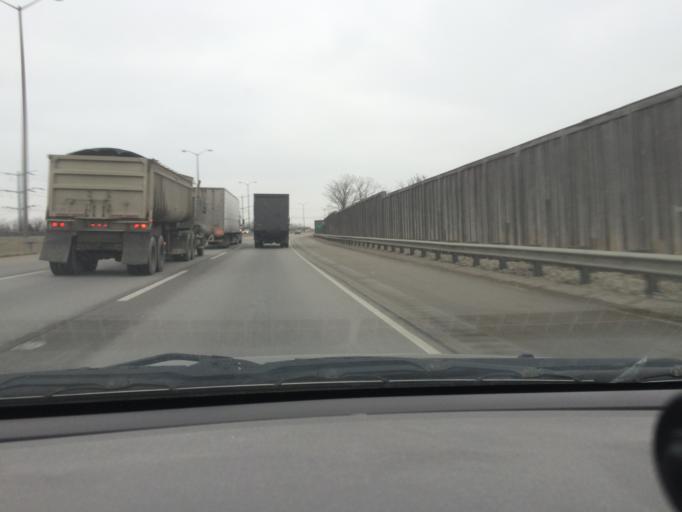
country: US
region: Illinois
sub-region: DuPage County
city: Glen Ellyn
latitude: 41.8579
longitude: -88.0413
